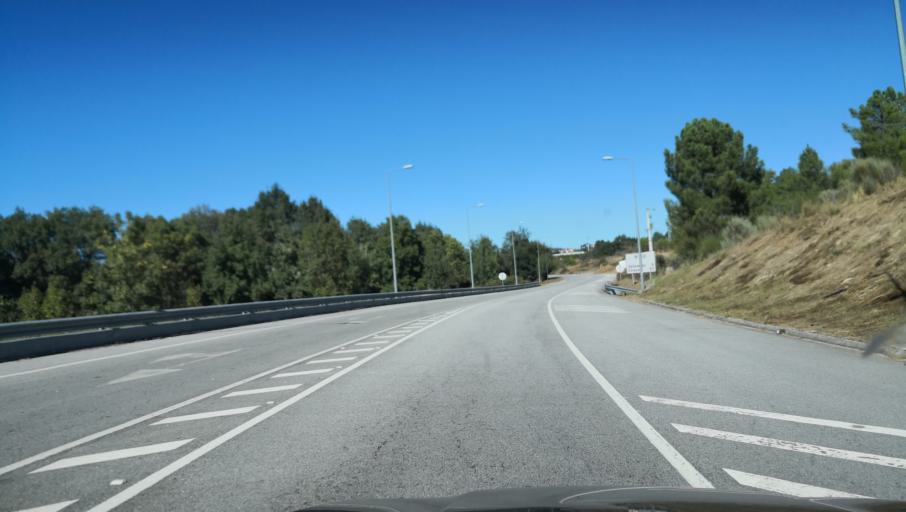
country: PT
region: Vila Real
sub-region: Valpacos
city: Valpacos
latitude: 41.5842
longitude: -7.3065
